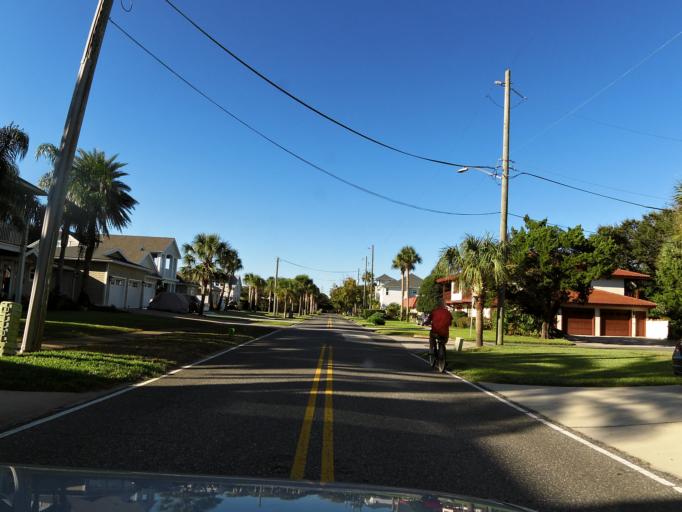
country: US
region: Florida
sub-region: Duval County
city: Atlantic Beach
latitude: 30.3376
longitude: -81.3987
